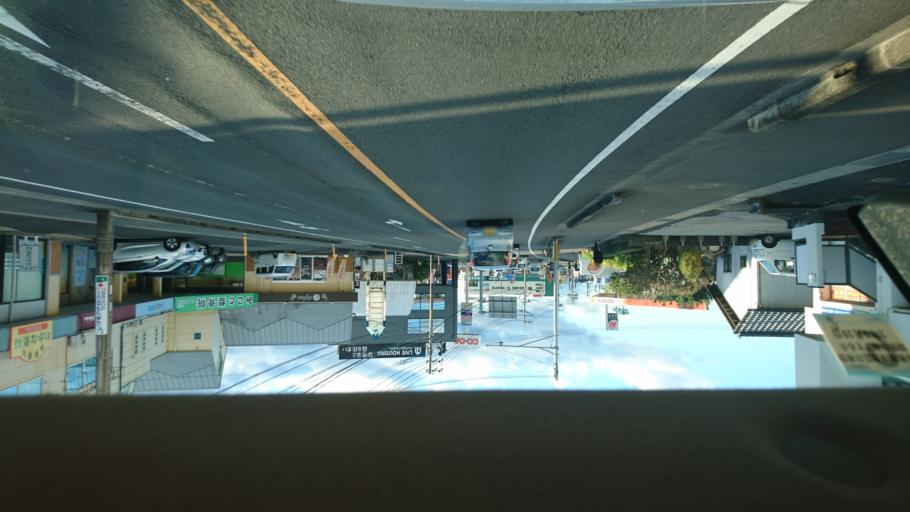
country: JP
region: Miyazaki
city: Miyazaki-shi
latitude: 31.8811
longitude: 131.4275
